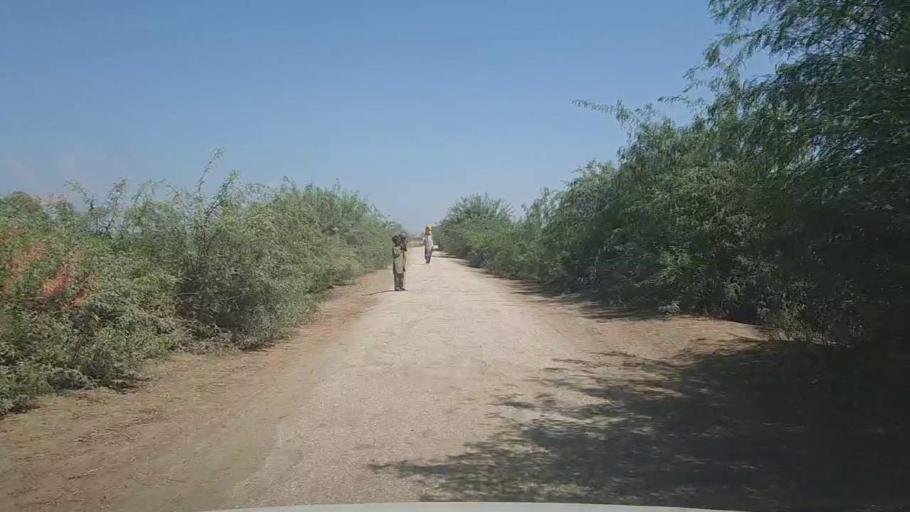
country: PK
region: Sindh
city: Kashmor
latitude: 28.2986
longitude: 69.4284
